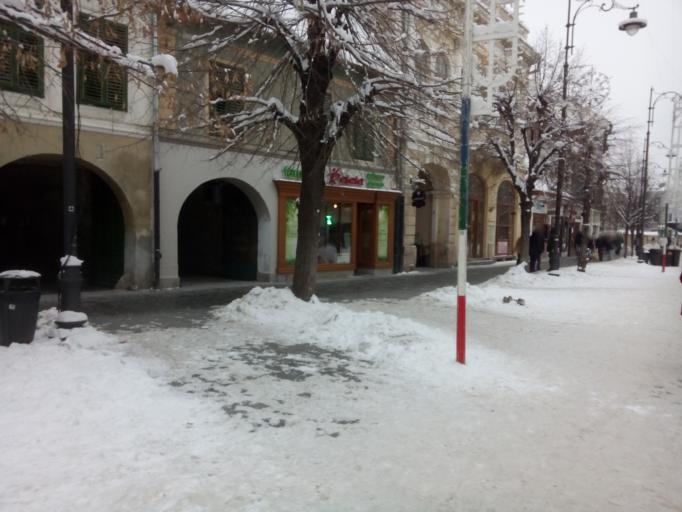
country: RO
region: Sibiu
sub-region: Municipiul Sibiu
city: Sibiu
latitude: 45.7938
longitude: 24.1499
